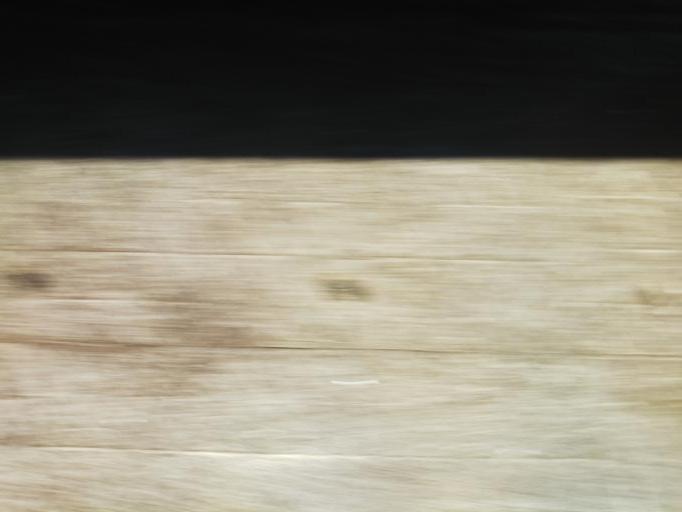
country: JP
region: Kochi
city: Nakamura
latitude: 33.0882
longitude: 133.1021
